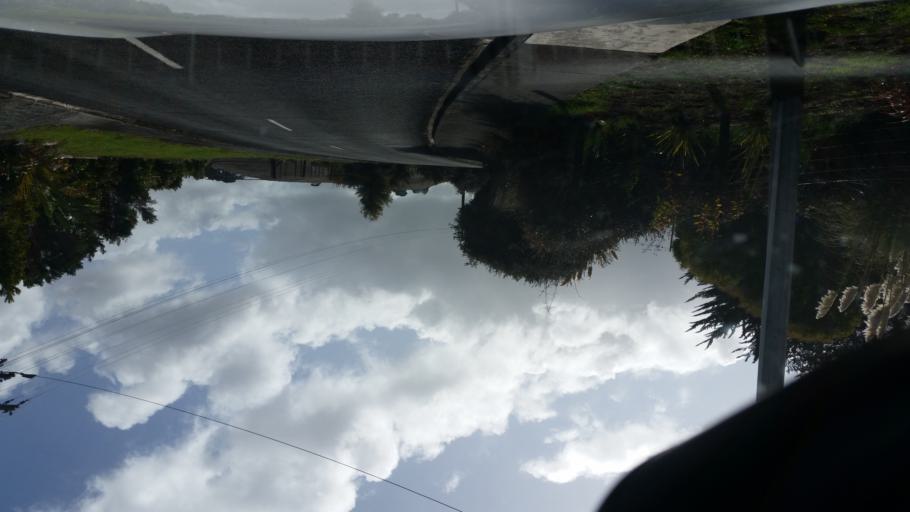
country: NZ
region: Northland
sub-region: Whangarei
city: Ruakaka
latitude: -36.1043
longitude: 174.3681
